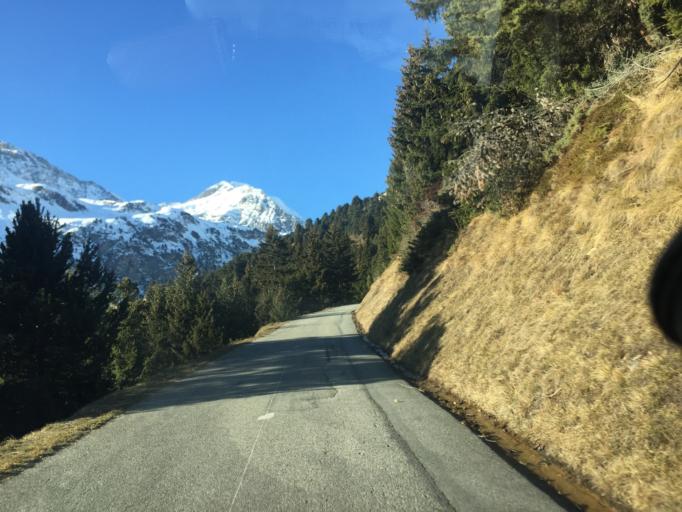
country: FR
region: Rhone-Alpes
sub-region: Departement de la Savoie
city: Modane
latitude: 45.2429
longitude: 6.7326
